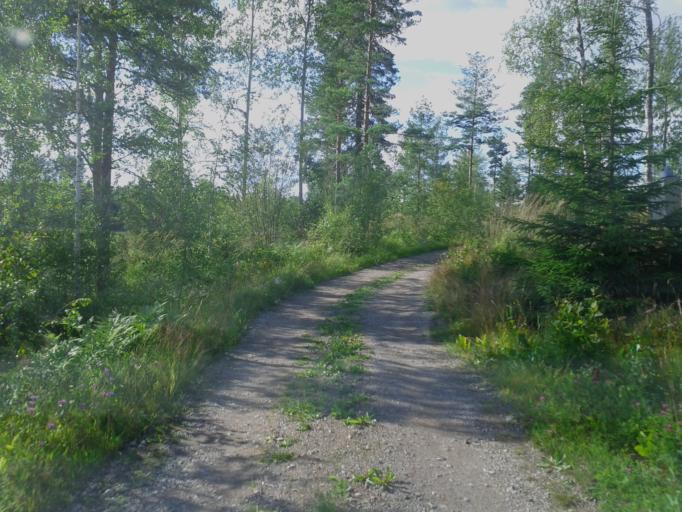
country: SE
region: Vaestmanland
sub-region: Sala Kommun
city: Sala
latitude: 59.9287
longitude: 16.4725
